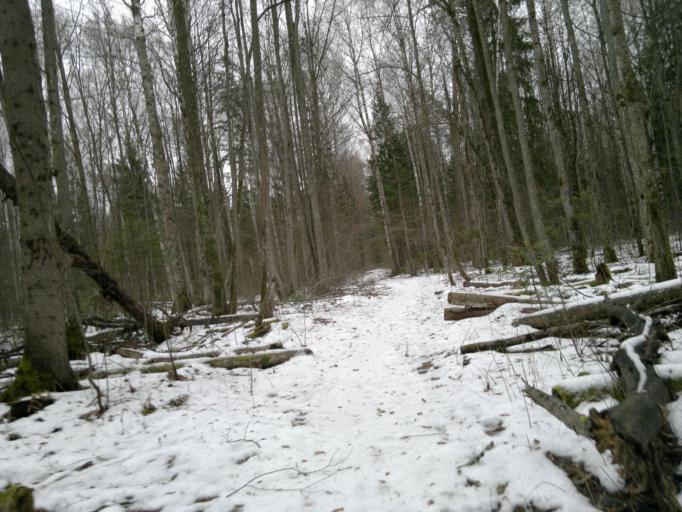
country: RU
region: Mariy-El
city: Yoshkar-Ola
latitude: 56.6116
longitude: 47.9399
